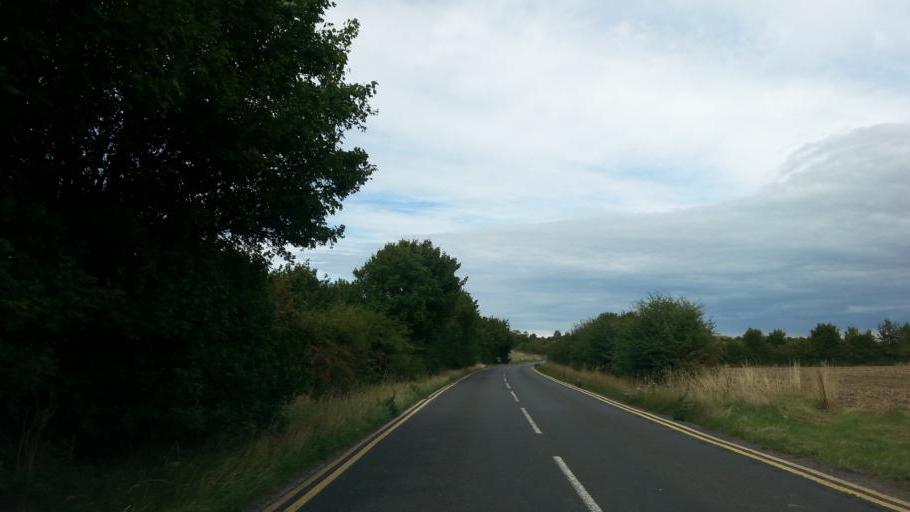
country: GB
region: England
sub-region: Cambridgeshire
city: Sawston
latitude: 52.1709
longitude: 0.1631
